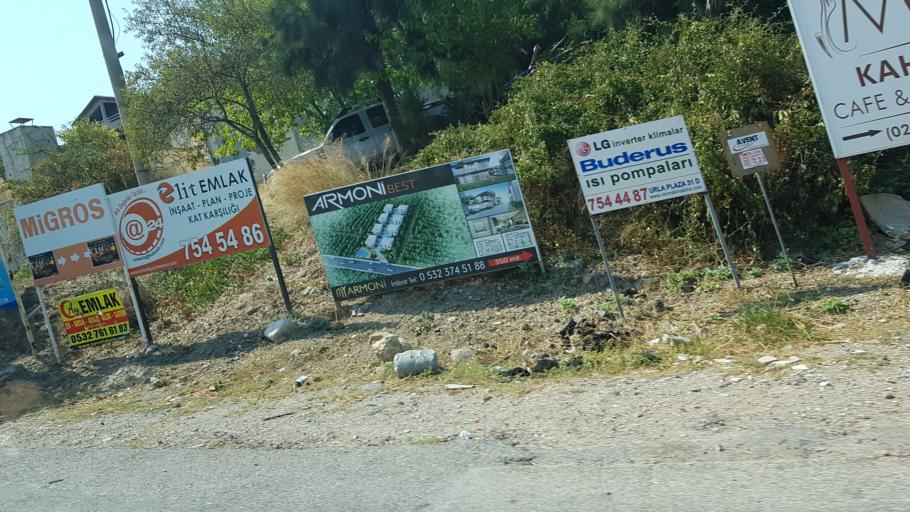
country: TR
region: Izmir
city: Urla
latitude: 38.3797
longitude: 26.7582
